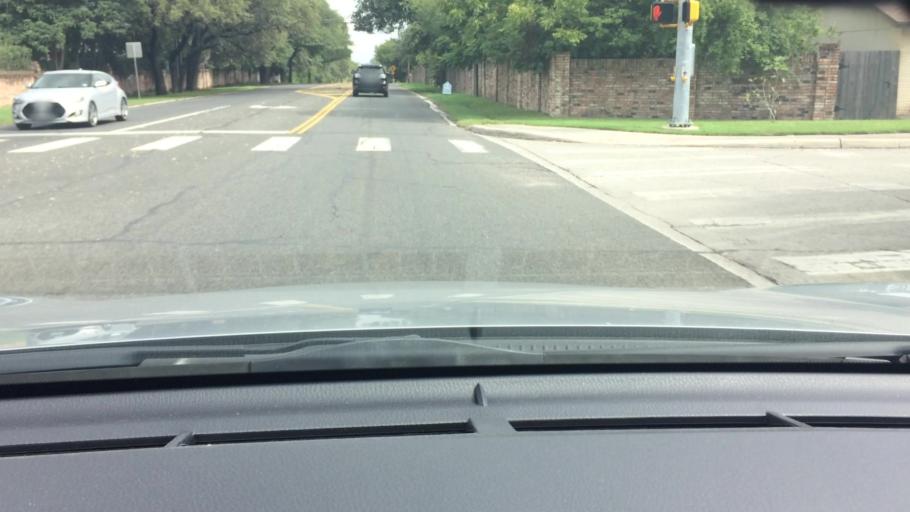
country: US
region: Texas
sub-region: Bexar County
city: Shavano Park
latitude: 29.5633
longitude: -98.5568
